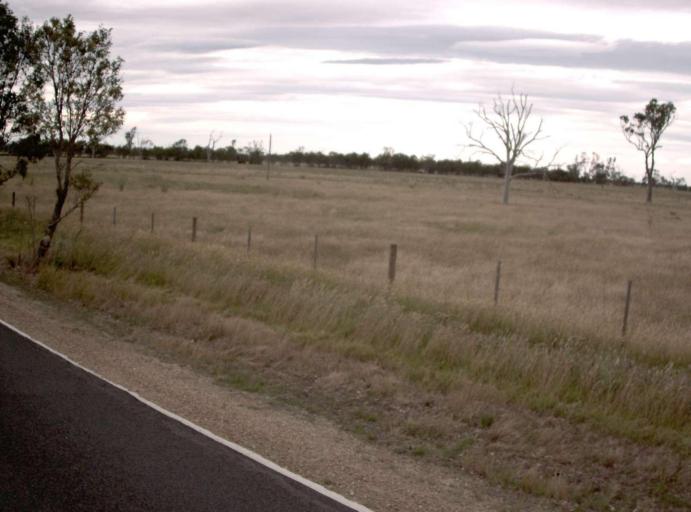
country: AU
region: Victoria
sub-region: Wellington
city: Sale
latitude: -37.9947
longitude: 147.1924
